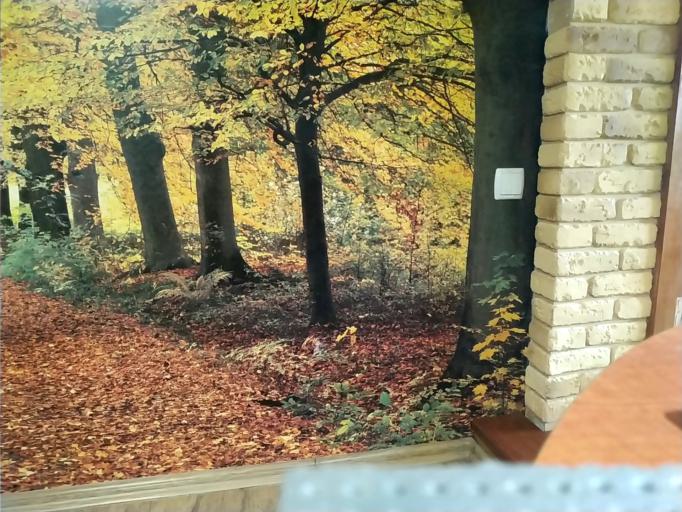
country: RU
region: Tverskaya
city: Kalashnikovo
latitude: 57.2740
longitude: 35.1940
